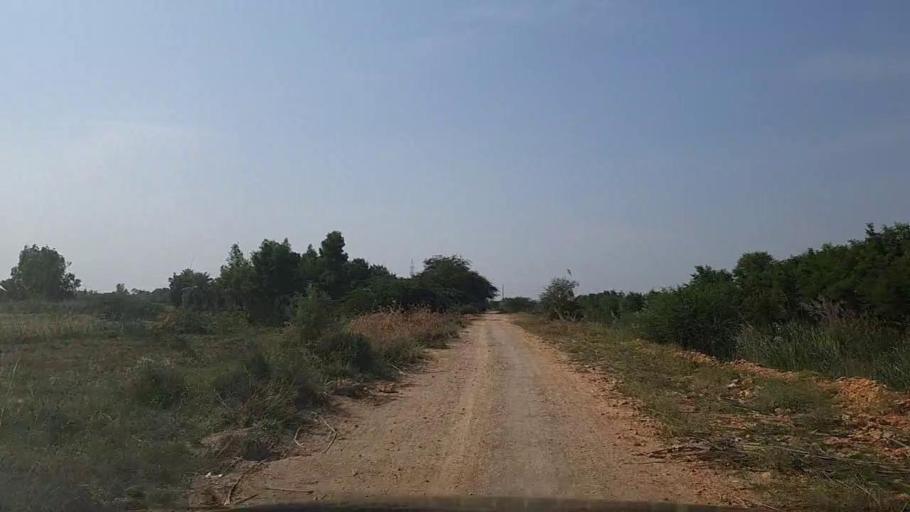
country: PK
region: Sindh
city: Thatta
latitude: 24.8059
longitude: 67.8504
